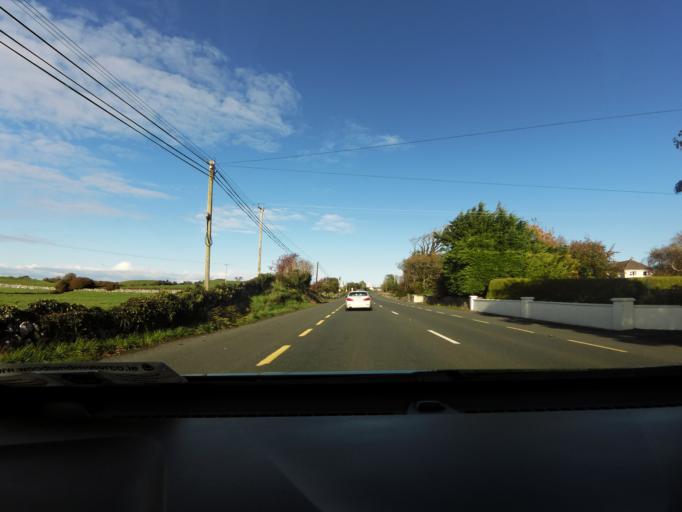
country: IE
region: Connaught
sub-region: County Galway
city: Moycullen
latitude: 53.4587
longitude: -9.1014
